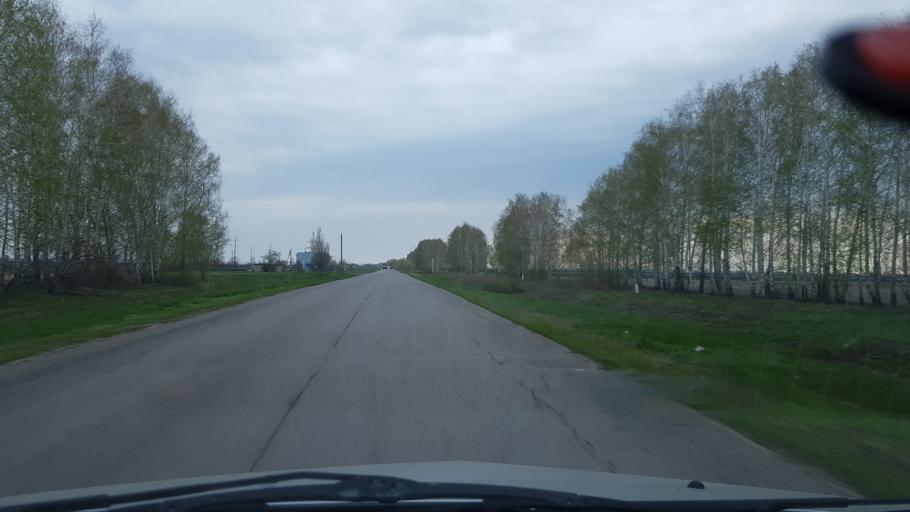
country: RU
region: Samara
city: Podstepki
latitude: 53.6657
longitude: 49.1669
